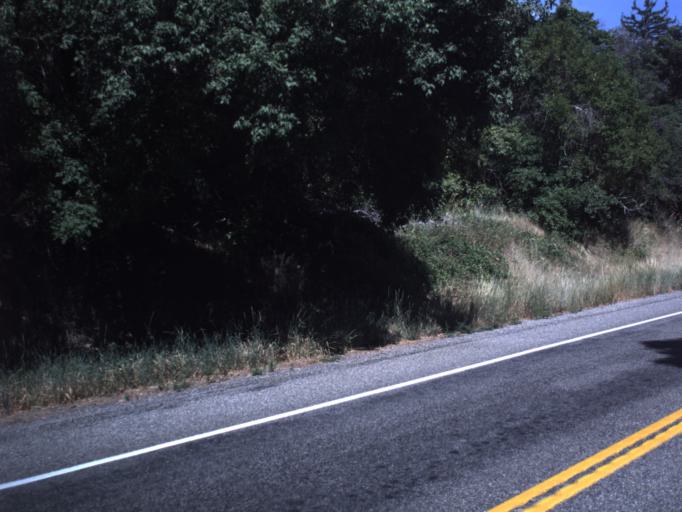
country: US
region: Utah
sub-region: Cache County
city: North Logan
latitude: 41.7631
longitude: -111.6960
